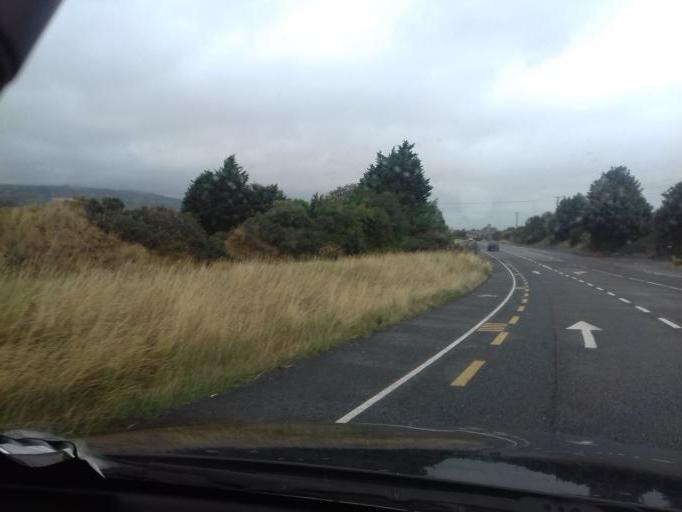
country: IE
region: Leinster
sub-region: County Carlow
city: Bagenalstown
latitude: 52.7615
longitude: -6.9559
